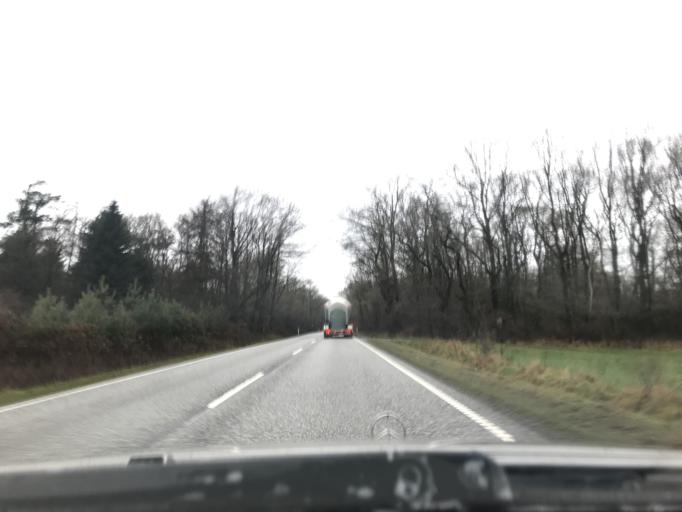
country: DK
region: South Denmark
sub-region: Haderslev Kommune
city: Gram
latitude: 55.2380
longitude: 8.9364
